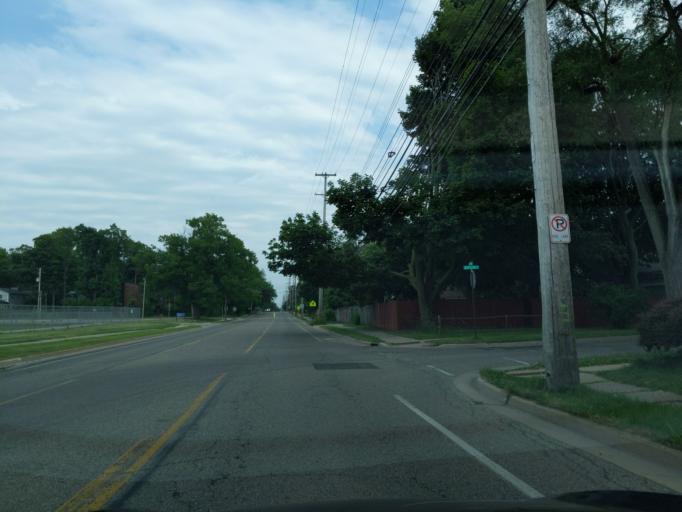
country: US
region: Michigan
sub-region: Ingham County
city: East Lansing
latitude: 42.7406
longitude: -84.4783
